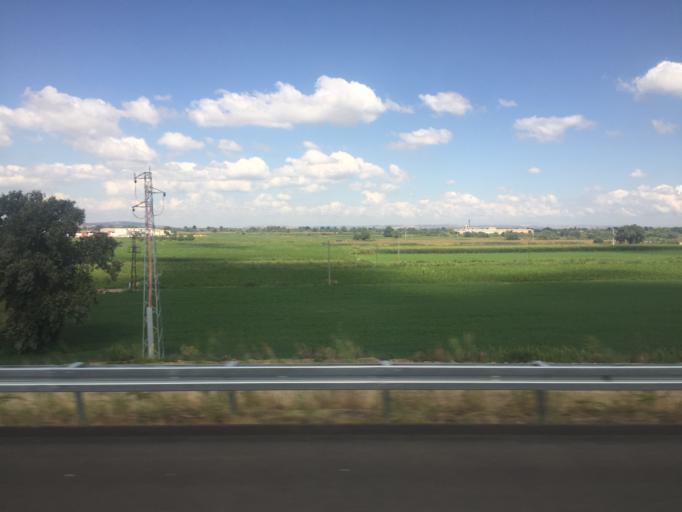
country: TR
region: Balikesir
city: Gobel
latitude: 40.0660
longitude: 28.2465
